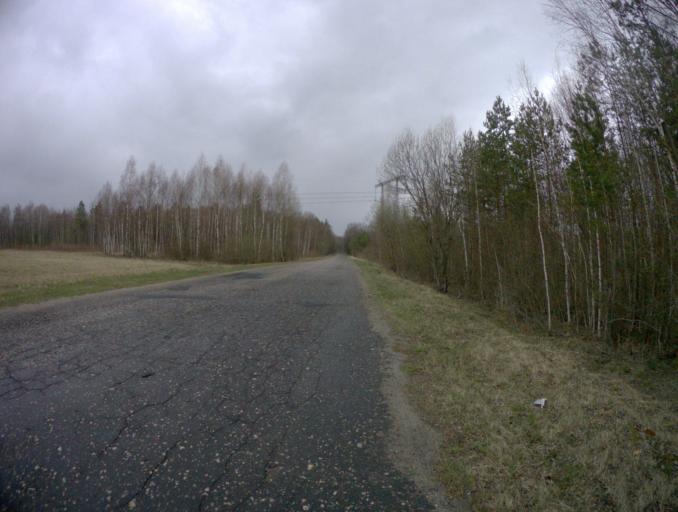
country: RU
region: Vladimir
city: Sudogda
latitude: 55.9665
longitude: 40.6879
